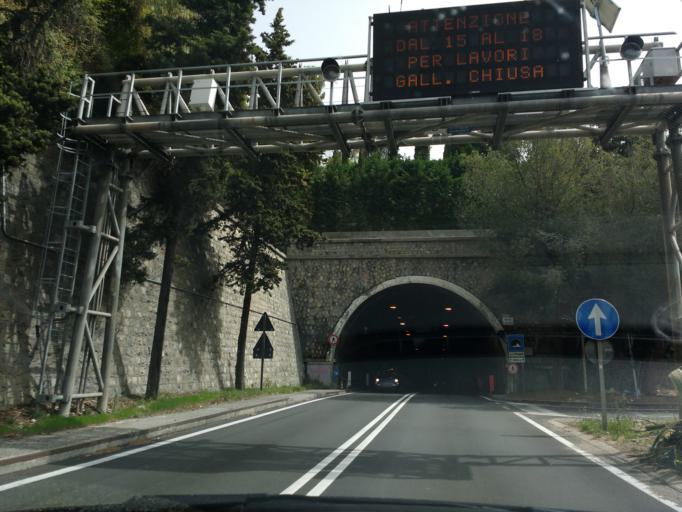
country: IT
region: Liguria
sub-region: Provincia di Imperia
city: Ventimiglia
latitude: 43.7935
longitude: 7.5834
